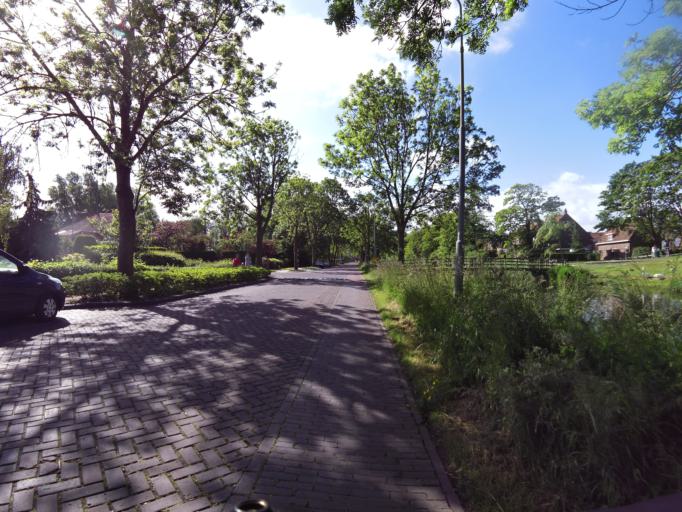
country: NL
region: Zeeland
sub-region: Schouwen-Duiveland
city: Scharendijke
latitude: 51.6512
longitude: 3.9252
